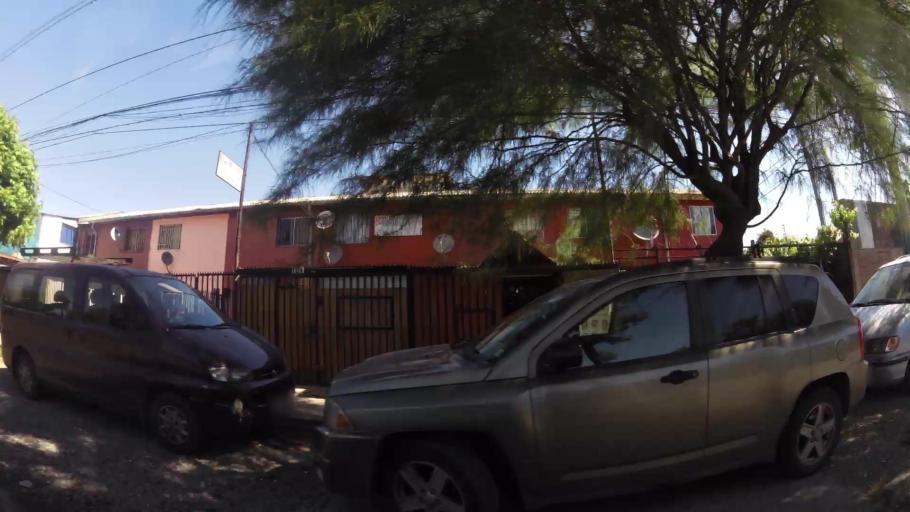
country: CL
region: Santiago Metropolitan
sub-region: Provincia de Maipo
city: San Bernardo
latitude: -33.5885
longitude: -70.6763
